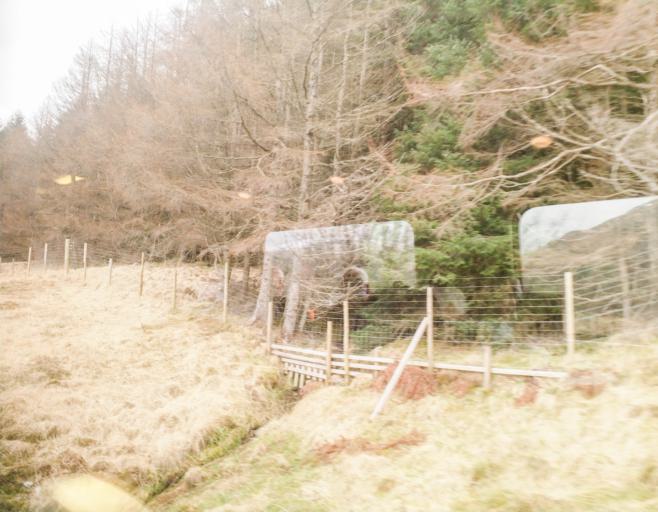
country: GB
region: Scotland
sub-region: Argyll and Bute
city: Garelochhead
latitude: 56.4376
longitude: -4.7060
